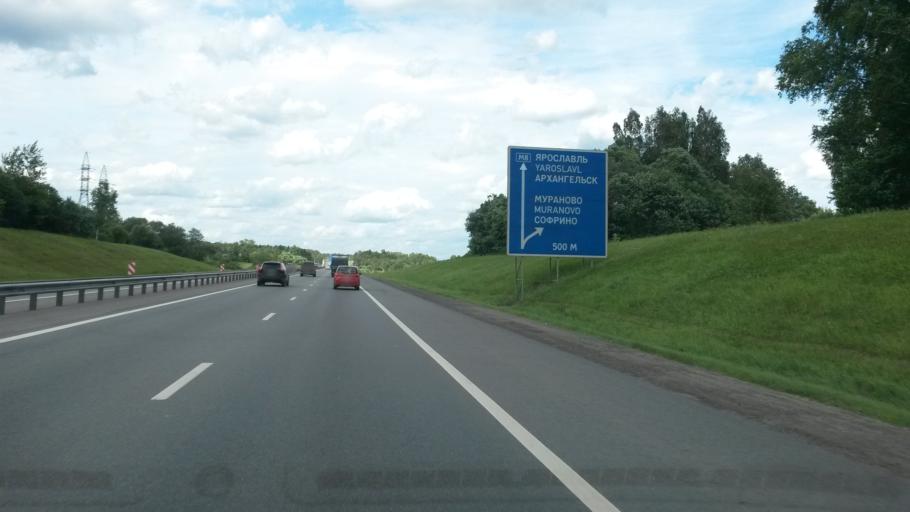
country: RU
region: Moskovskaya
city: Ashukino
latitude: 56.1285
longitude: 37.9904
